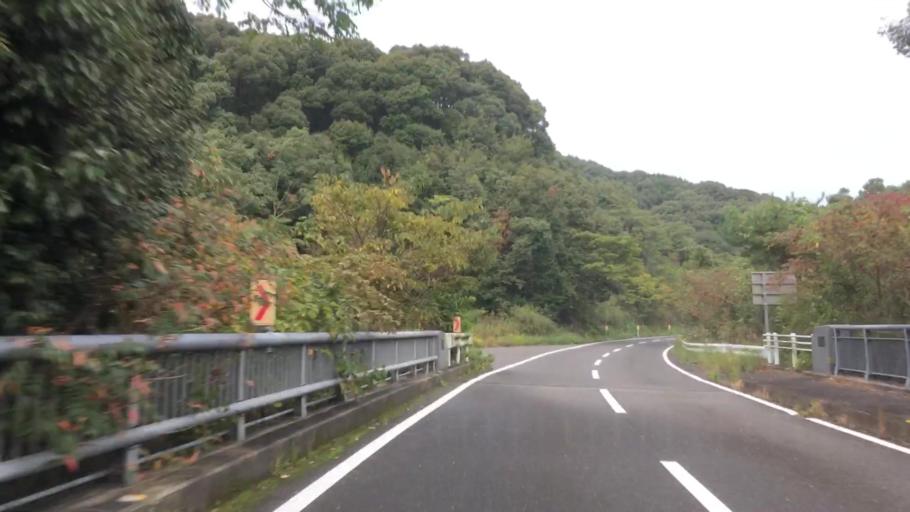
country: JP
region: Nagasaki
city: Sasebo
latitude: 32.9976
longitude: 129.7088
